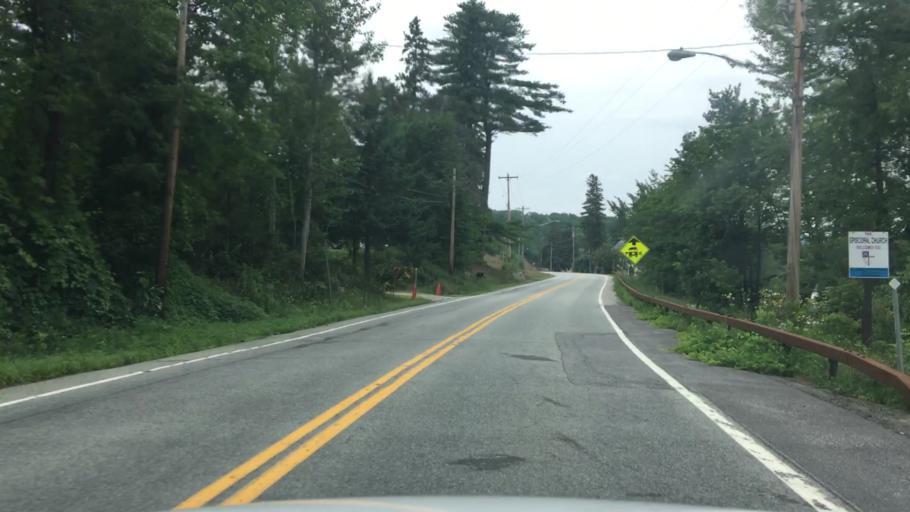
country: US
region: New York
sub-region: Clinton County
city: Peru
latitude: 44.4300
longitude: -73.6800
